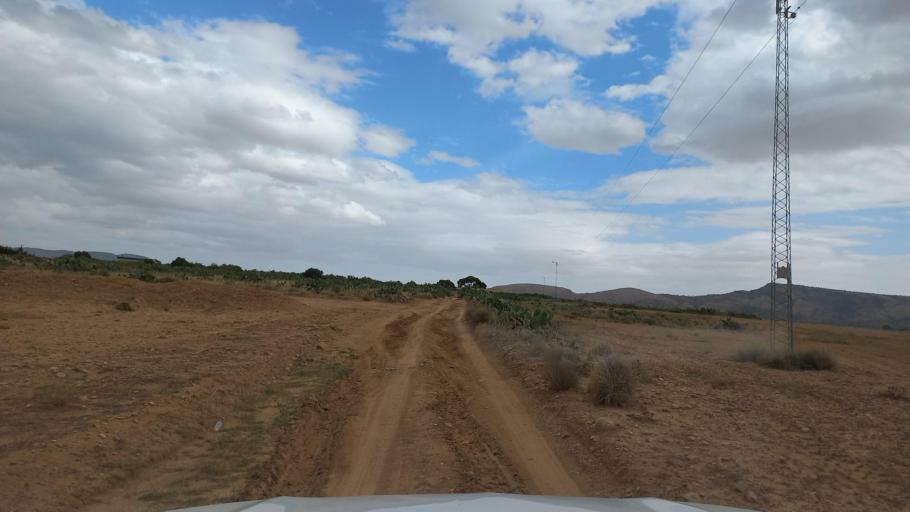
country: TN
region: Al Qasrayn
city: Sbiba
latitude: 35.3789
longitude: 9.1261
